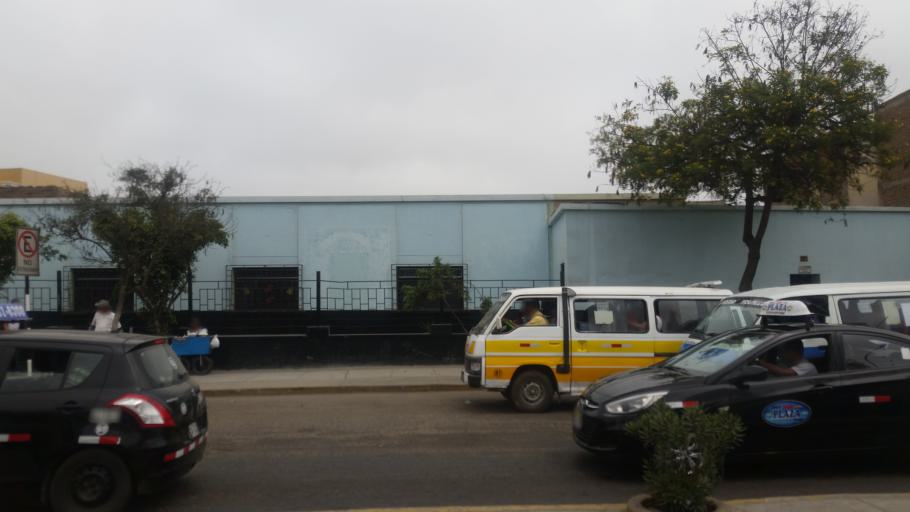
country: PE
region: La Libertad
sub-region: Provincia de Trujillo
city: Trujillo
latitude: -8.1159
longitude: -79.0308
